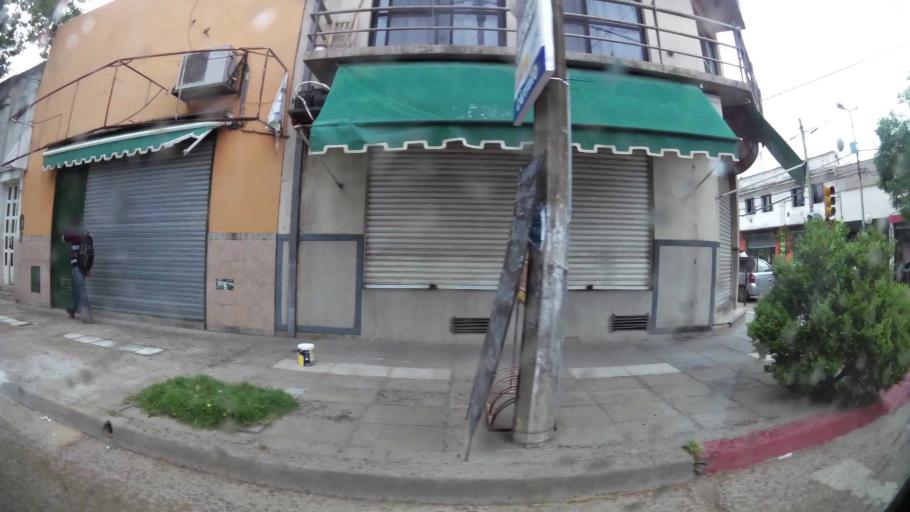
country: AR
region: Buenos Aires
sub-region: Partido de Zarate
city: Zarate
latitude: -34.0950
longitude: -59.0256
